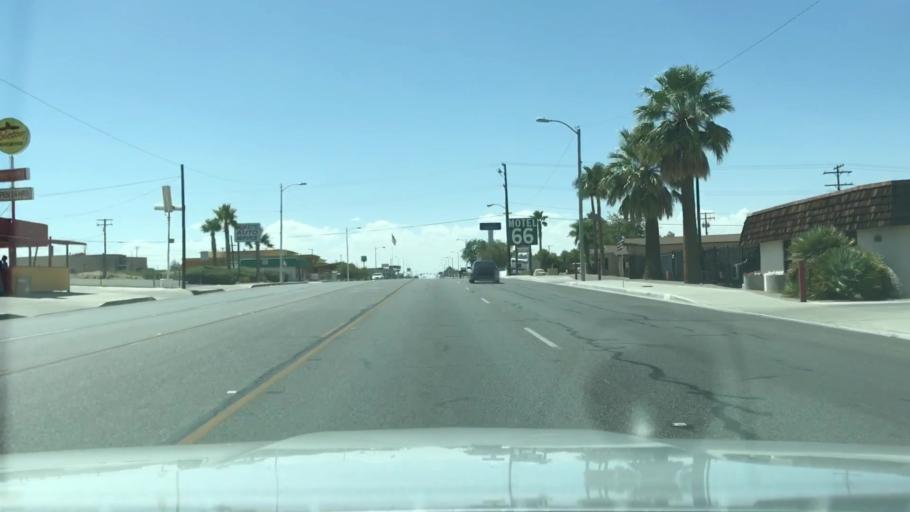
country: US
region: California
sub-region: San Bernardino County
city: Barstow Heights
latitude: 34.8939
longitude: -117.0484
